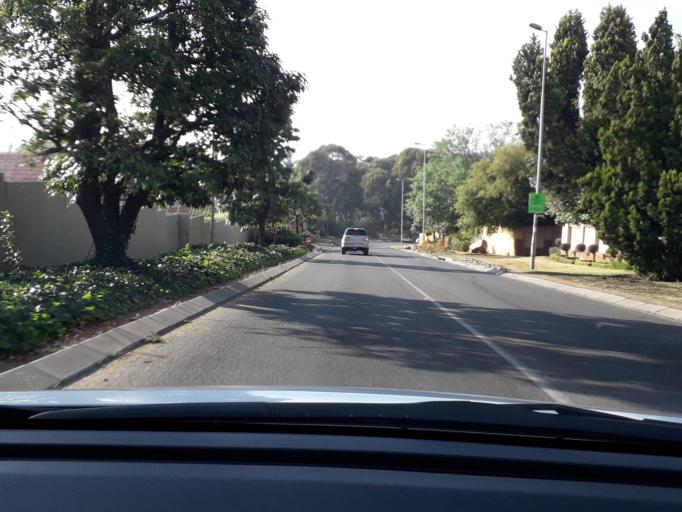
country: ZA
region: Gauteng
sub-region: West Rand District Municipality
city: Muldersdriseloop
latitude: -26.0711
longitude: 27.9456
